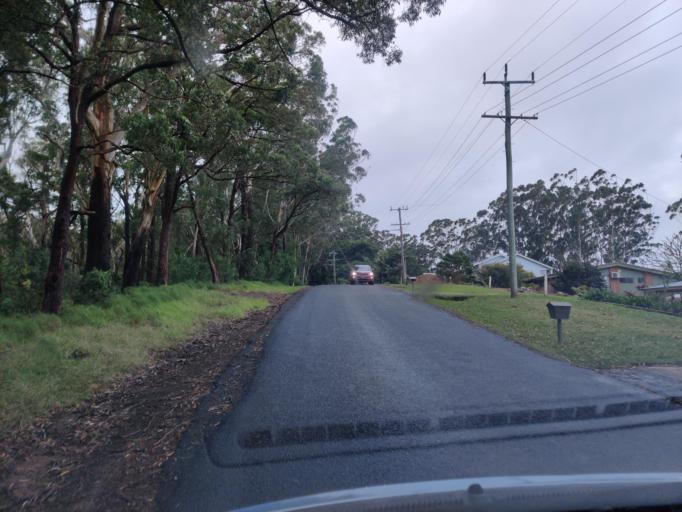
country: AU
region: New South Wales
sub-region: Great Lakes
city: Forster
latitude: -32.3848
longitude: 152.5038
